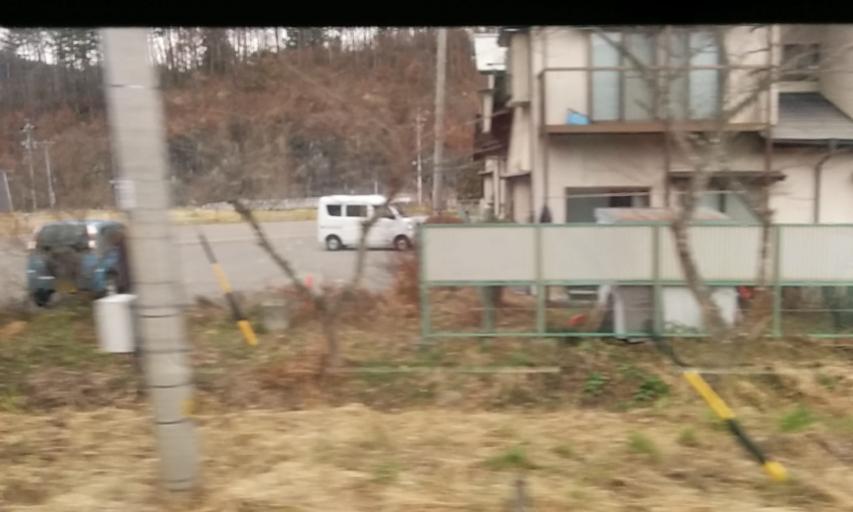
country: JP
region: Nagano
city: Hotaka
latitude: 36.3996
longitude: 138.0113
